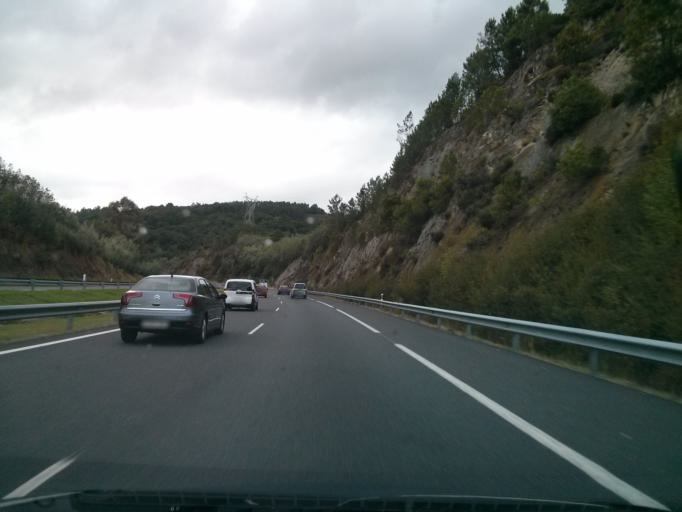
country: ES
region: Galicia
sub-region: Provincia de Ourense
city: Castrelo de Mino
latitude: 42.3352
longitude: -8.0471
